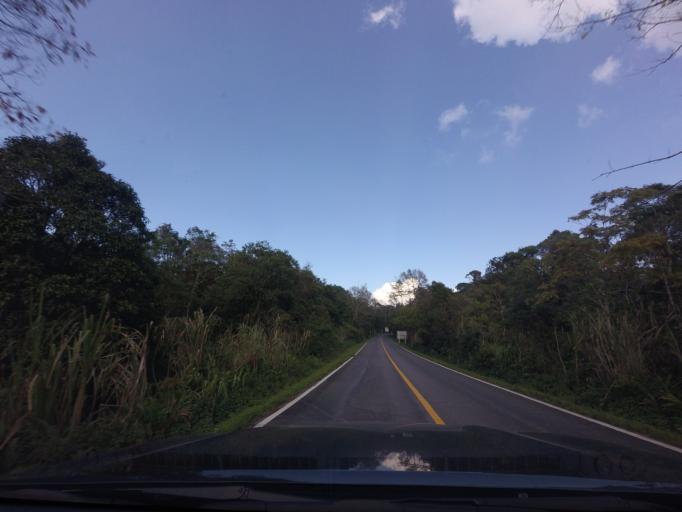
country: TH
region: Phetchabun
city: Lom Kao
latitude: 16.9444
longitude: 101.0329
